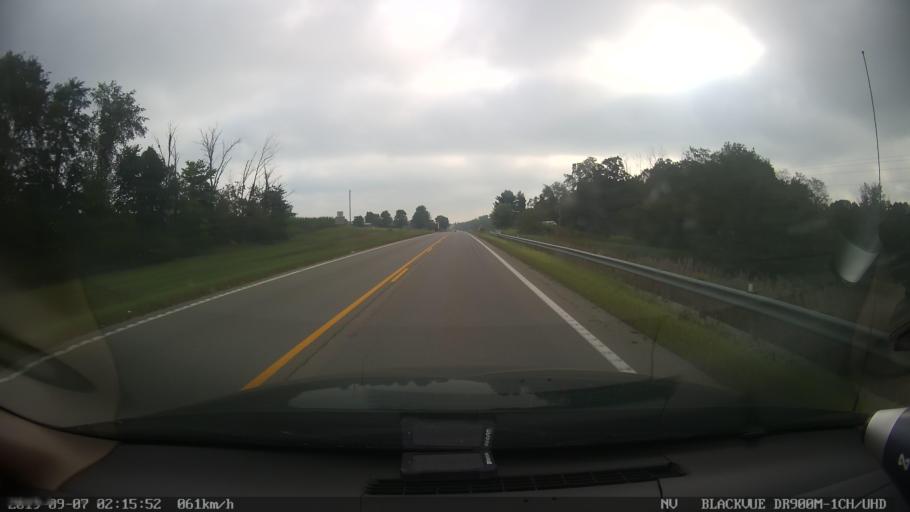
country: US
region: Ohio
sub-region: Licking County
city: Utica
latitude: 40.2168
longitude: -82.5472
